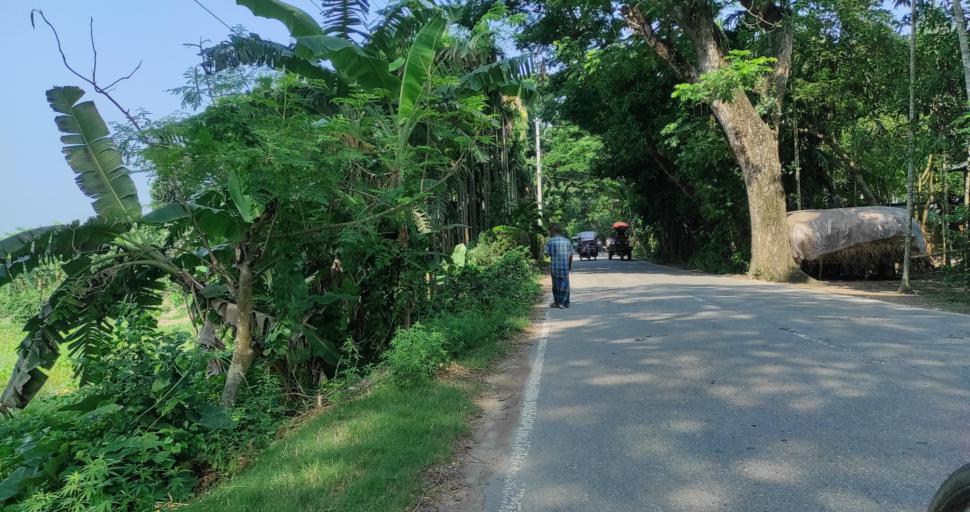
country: BD
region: Rajshahi
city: Ishurdi
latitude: 24.2887
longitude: 89.0720
